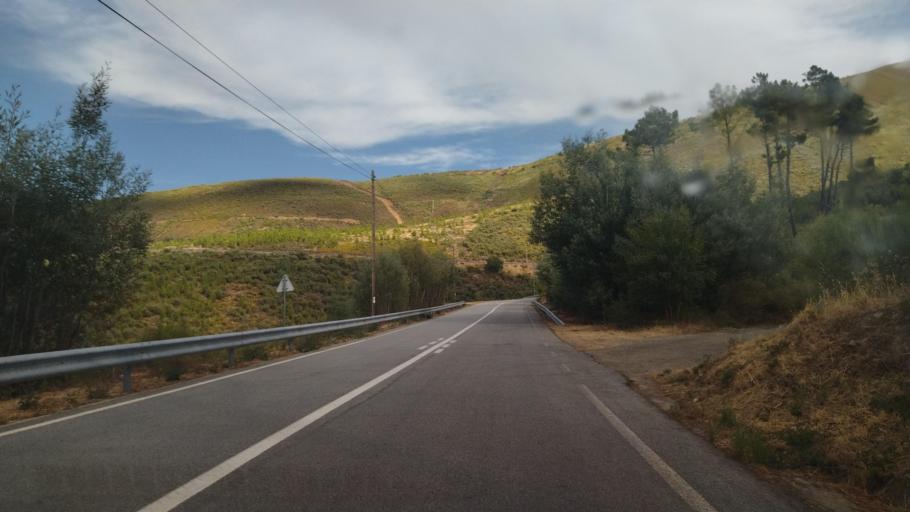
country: PT
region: Castelo Branco
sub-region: Covilha
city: Teixoso
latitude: 40.3711
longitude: -7.4551
